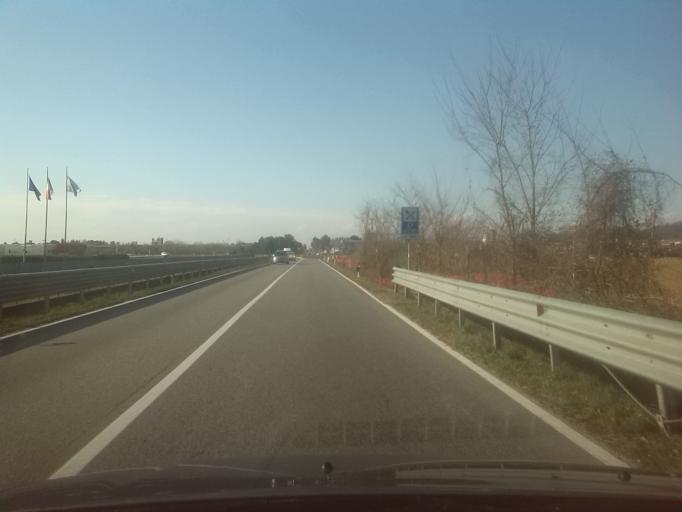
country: IT
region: Friuli Venezia Giulia
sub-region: Provincia di Udine
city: Manzano
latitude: 45.9806
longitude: 13.3835
